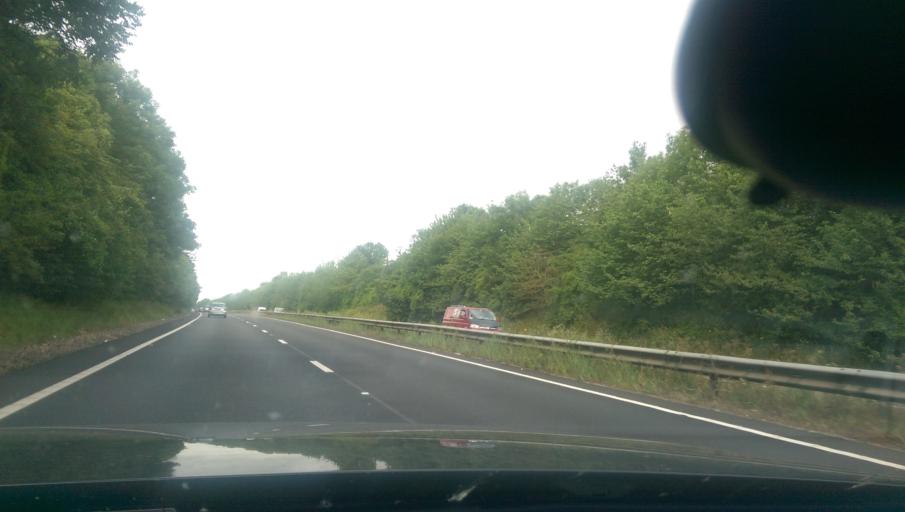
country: GB
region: England
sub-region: Hampshire
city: Abbotts Ann
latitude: 51.2127
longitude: -1.5639
